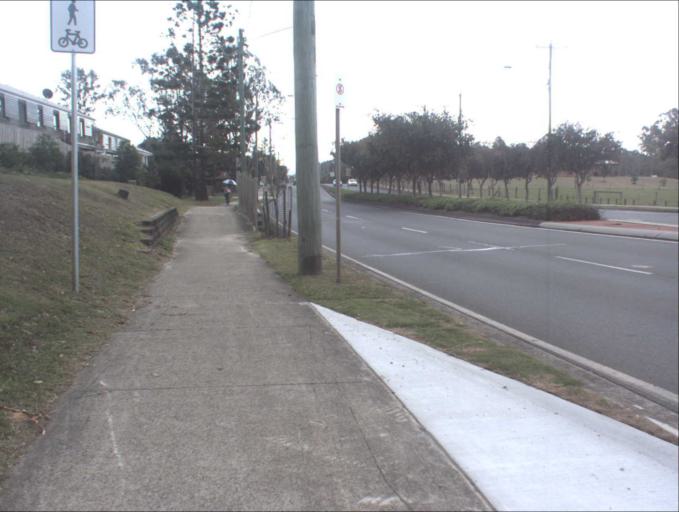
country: AU
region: Queensland
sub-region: Logan
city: Waterford West
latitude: -27.6822
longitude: 153.1370
